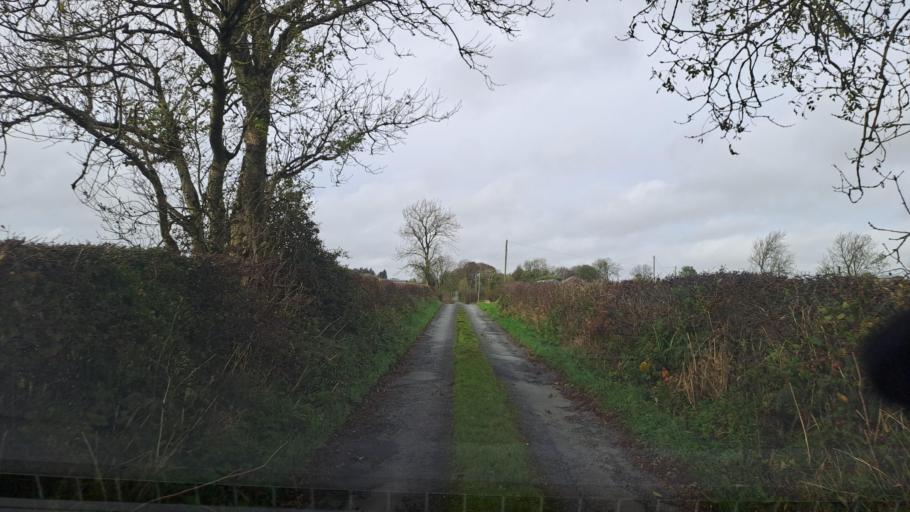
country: IE
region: Ulster
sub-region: County Monaghan
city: Carrickmacross
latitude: 54.0114
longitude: -6.7999
